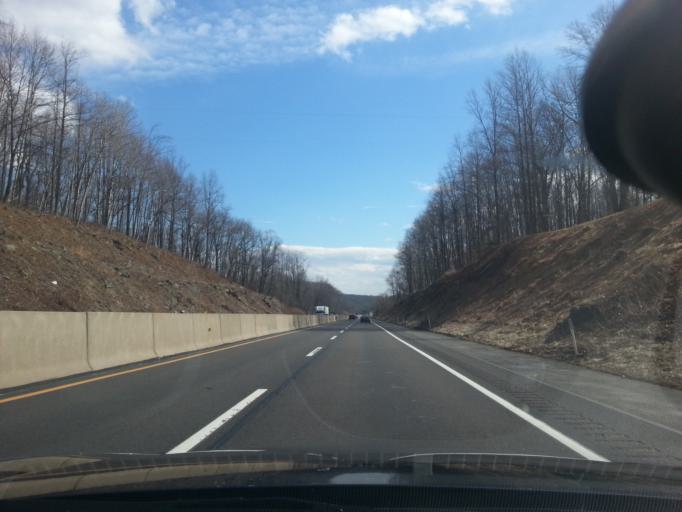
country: US
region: Pennsylvania
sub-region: Bucks County
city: Spinnerstown
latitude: 40.3802
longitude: -75.4075
